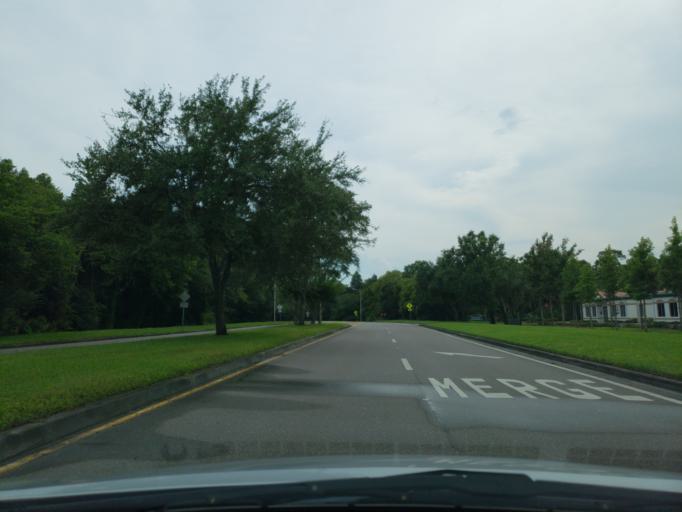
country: US
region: Florida
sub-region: Hillsborough County
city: Temple Terrace
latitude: 28.0673
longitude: -82.3750
